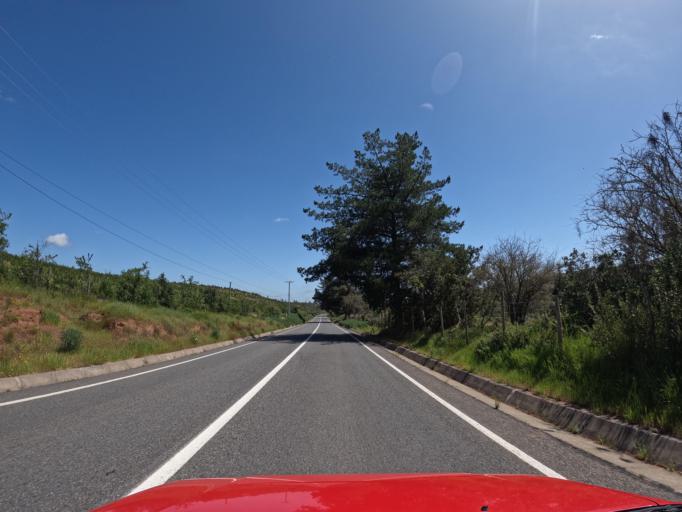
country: CL
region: O'Higgins
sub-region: Provincia de Colchagua
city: Santa Cruz
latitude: -34.6655
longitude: -71.8301
